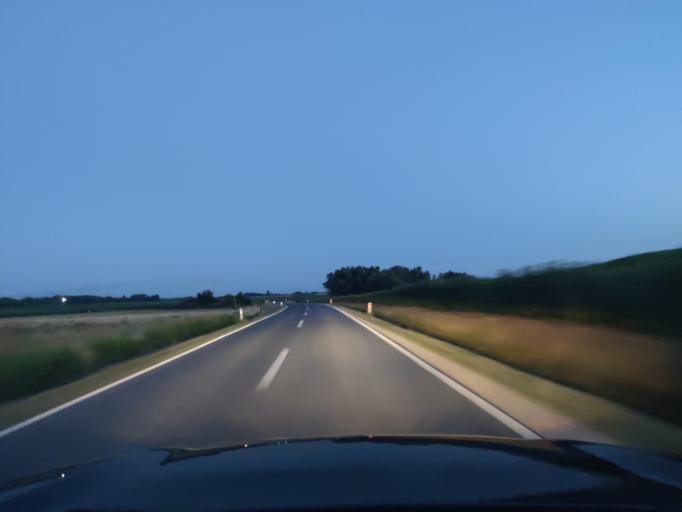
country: HR
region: Medimurska
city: Vratisinec
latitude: 46.4888
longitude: 16.4255
